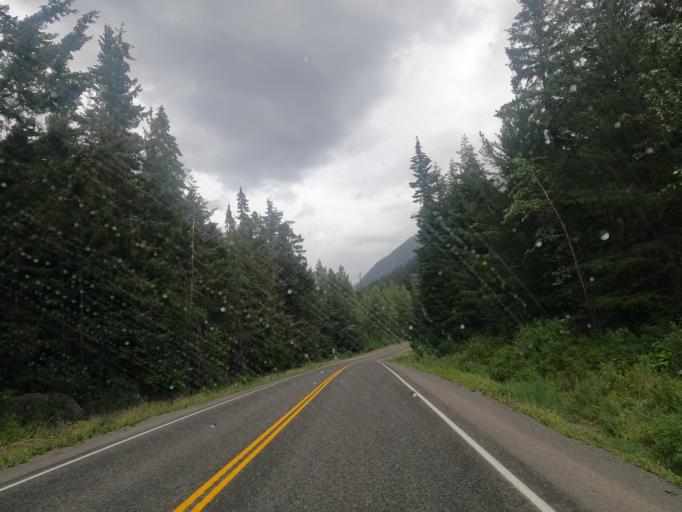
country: CA
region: British Columbia
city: Lillooet
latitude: 50.4768
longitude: -122.2229
